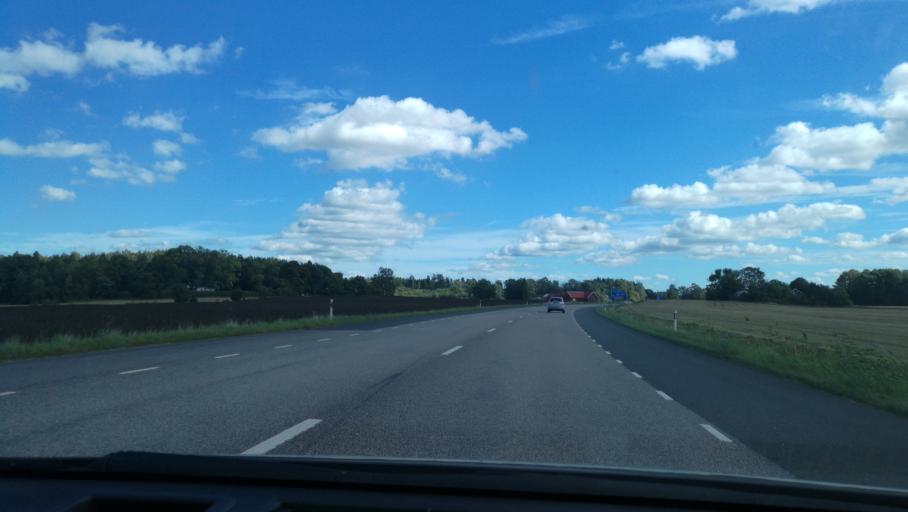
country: SE
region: Vaestra Goetaland
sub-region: Gotene Kommun
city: Kallby
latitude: 58.5115
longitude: 13.3373
